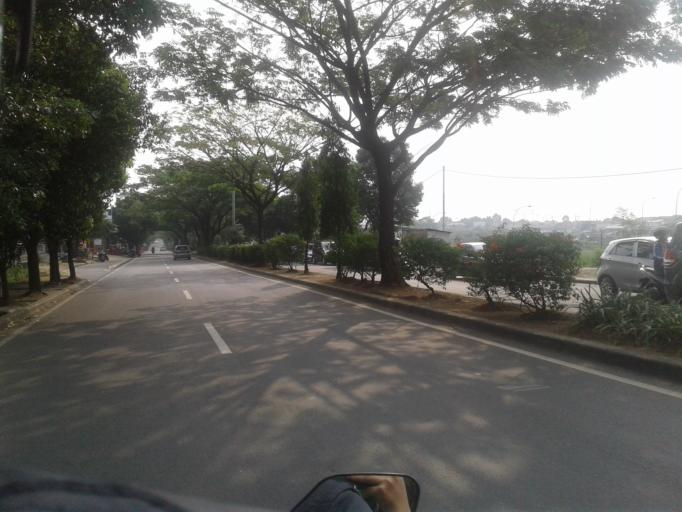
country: ID
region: West Java
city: Depok
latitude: -6.3820
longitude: 106.8653
